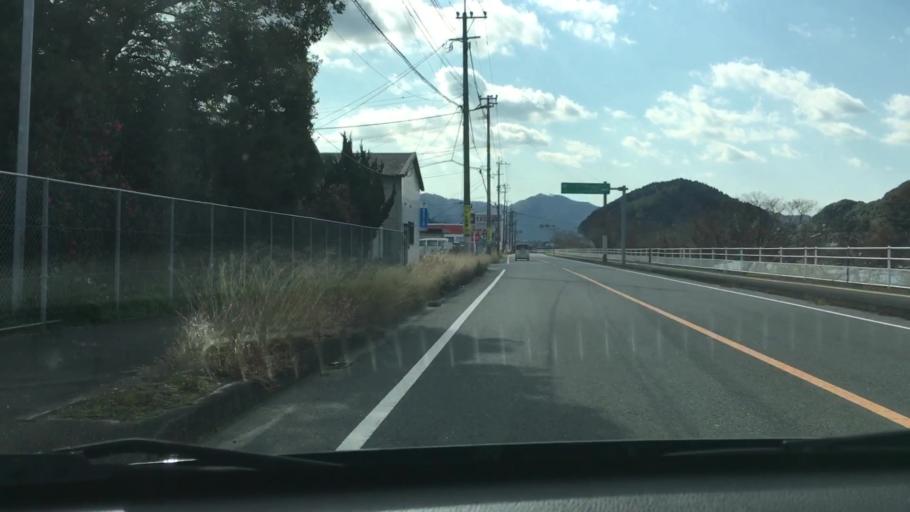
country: JP
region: Oita
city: Saiki
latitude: 32.9678
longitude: 131.9156
